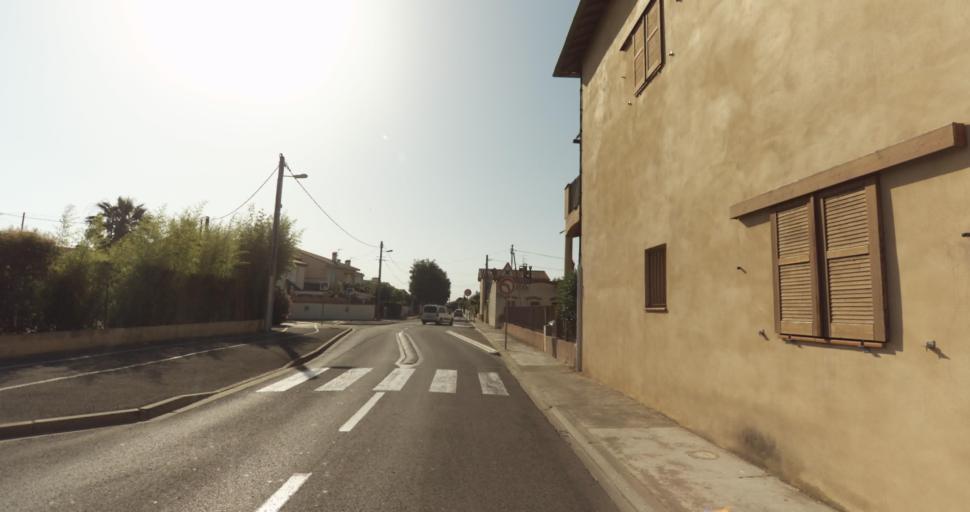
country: FR
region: Languedoc-Roussillon
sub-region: Departement des Pyrenees-Orientales
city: Alenya
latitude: 42.6407
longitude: 2.9823
